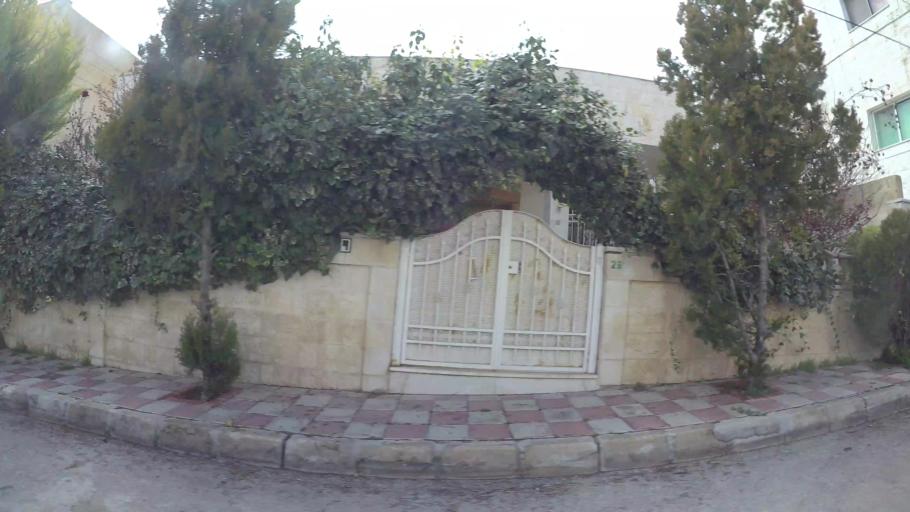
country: JO
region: Amman
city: Al Jubayhah
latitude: 32.0610
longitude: 35.8752
